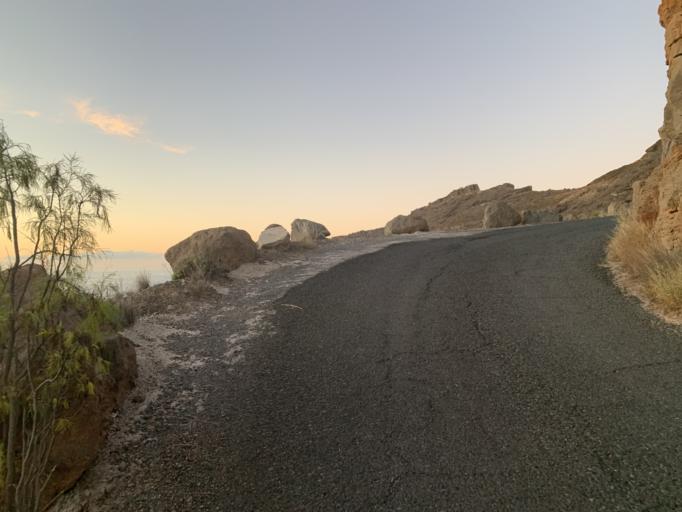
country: ES
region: Canary Islands
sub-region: Provincia de Las Palmas
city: Puerto Rico
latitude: 27.8063
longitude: -15.7314
